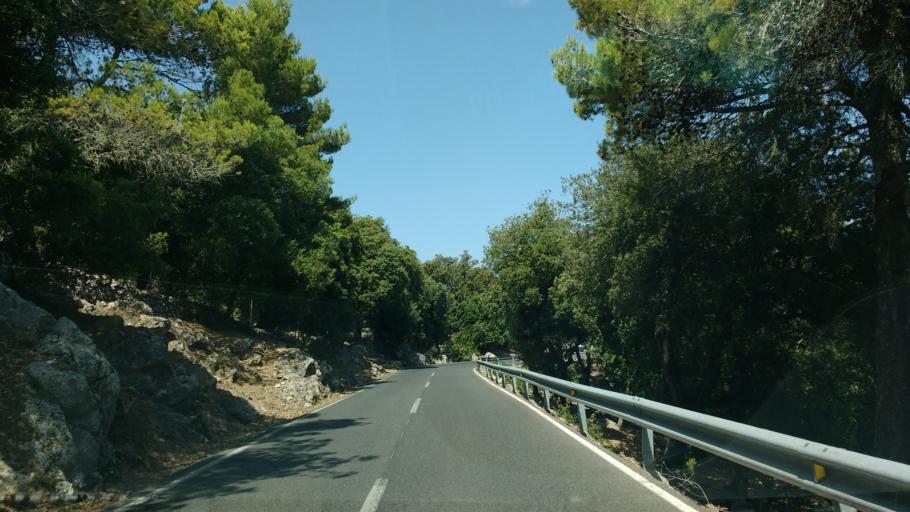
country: ES
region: Balearic Islands
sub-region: Illes Balears
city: Escorca
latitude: 39.8254
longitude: 2.8487
